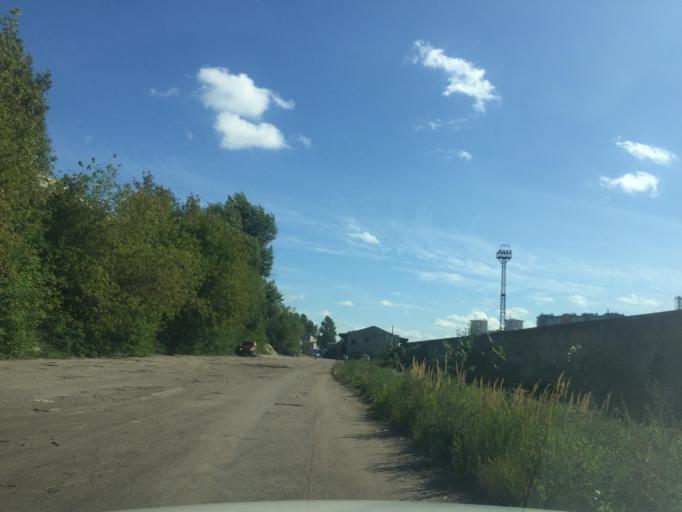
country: RU
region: St.-Petersburg
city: Kushelevka
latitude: 59.9914
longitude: 30.3573
